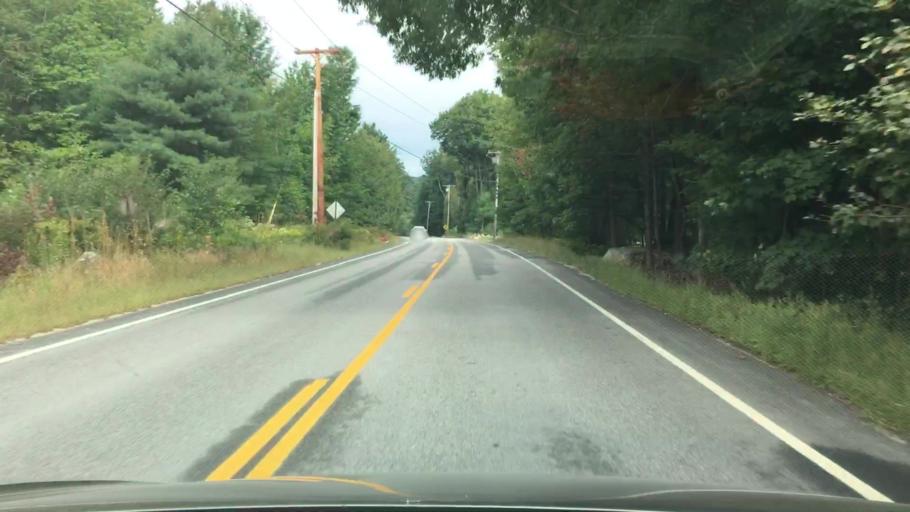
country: US
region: Maine
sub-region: Androscoggin County
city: Livermore
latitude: 44.3375
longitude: -70.2928
